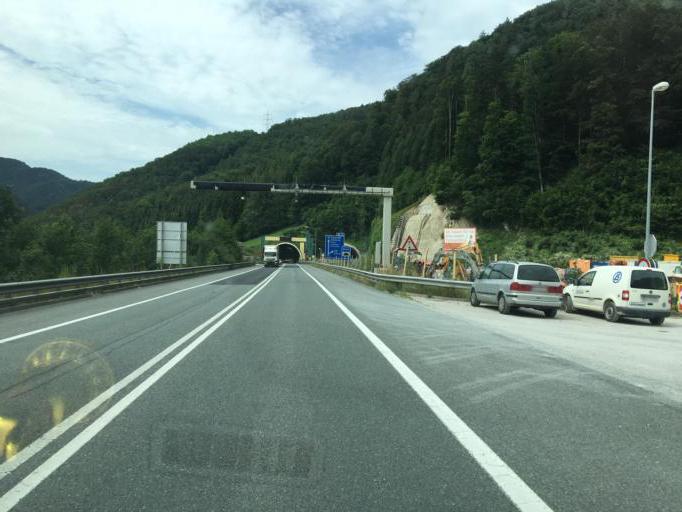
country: AT
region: Upper Austria
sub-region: Politischer Bezirk Kirchdorf an der Krems
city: Micheldorf in Oberoesterreich
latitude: 47.8184
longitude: 14.1689
